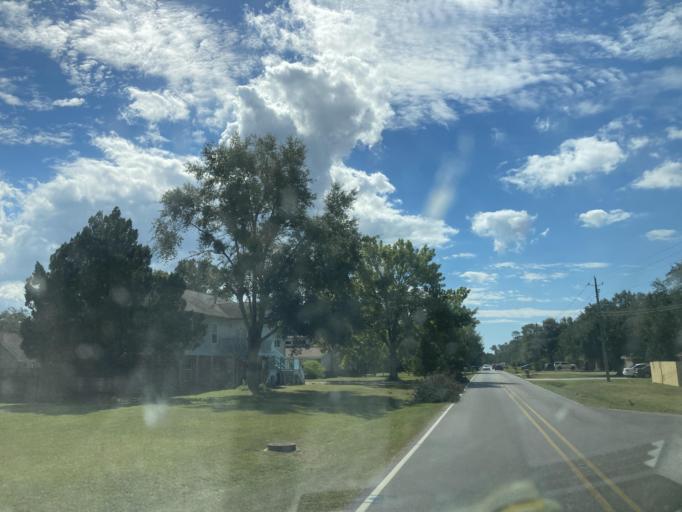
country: US
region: Mississippi
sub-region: Jackson County
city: Saint Martin
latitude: 30.4389
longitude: -88.8539
